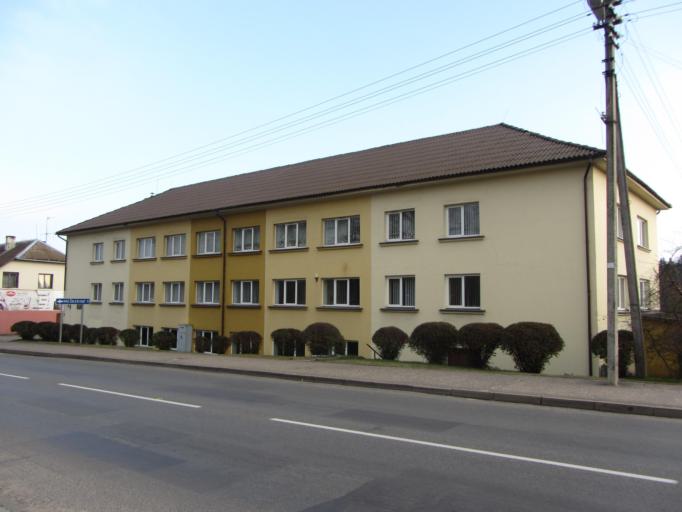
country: LT
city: Pabrade
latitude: 54.9832
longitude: 25.7702
